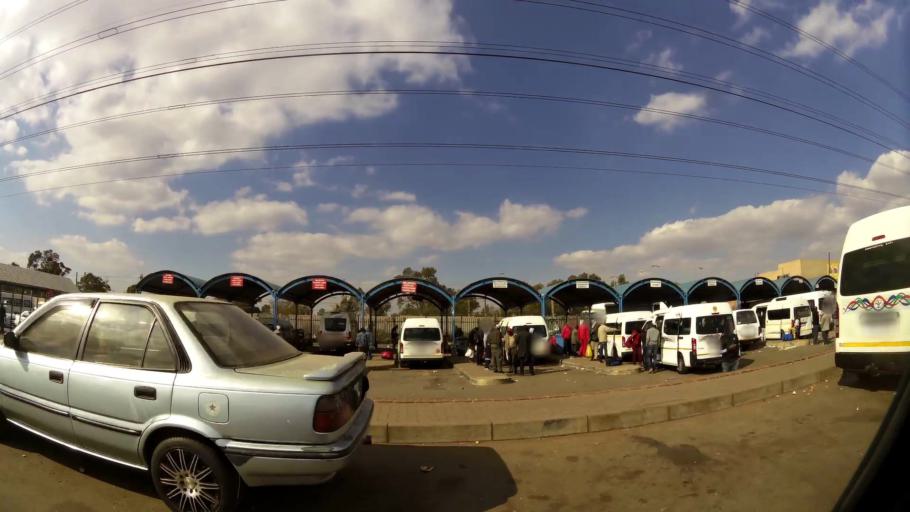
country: ZA
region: Gauteng
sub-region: Ekurhuleni Metropolitan Municipality
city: Tembisa
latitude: -26.0047
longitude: 28.2476
